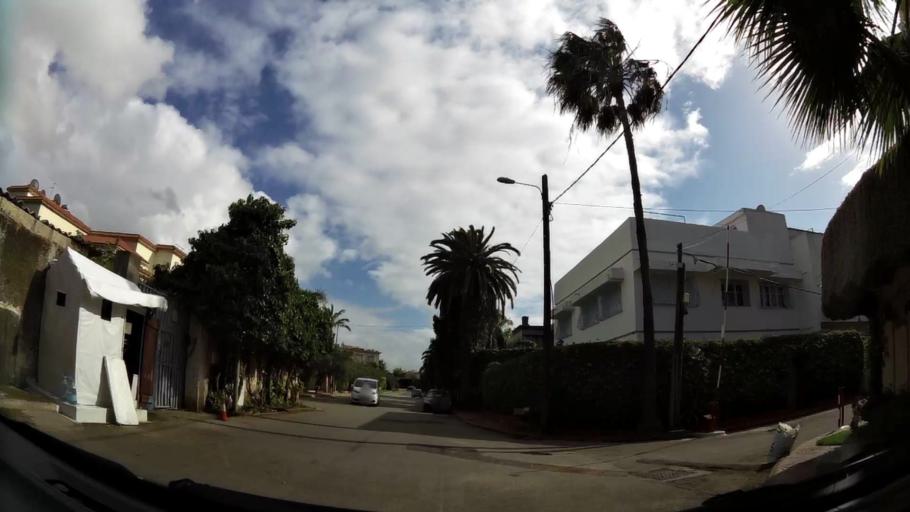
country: MA
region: Grand Casablanca
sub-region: Casablanca
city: Casablanca
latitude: 33.5442
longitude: -7.6254
